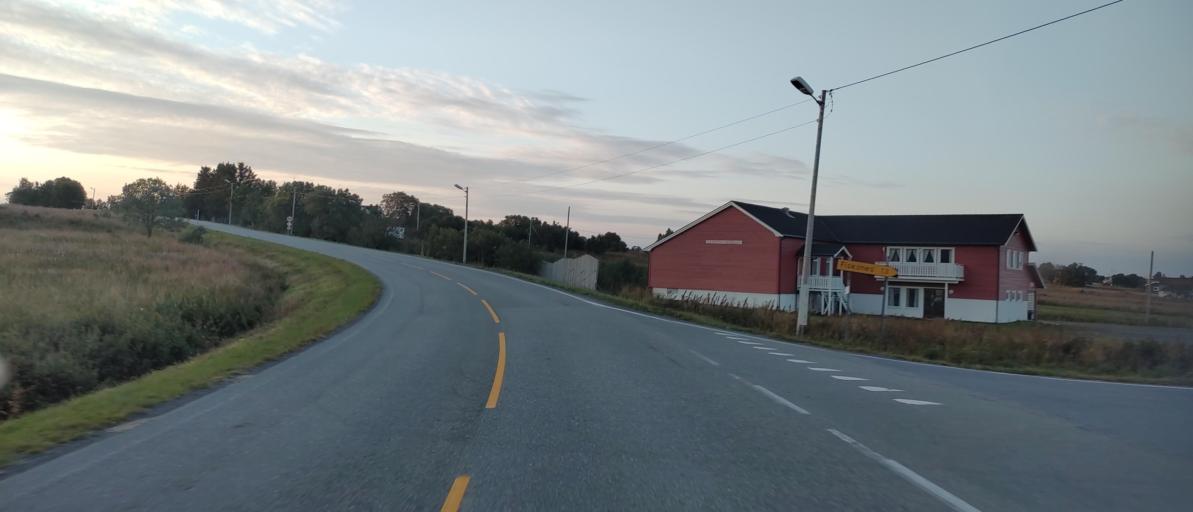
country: NO
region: Nordland
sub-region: Andoy
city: Andenes
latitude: 69.2445
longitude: 16.1188
